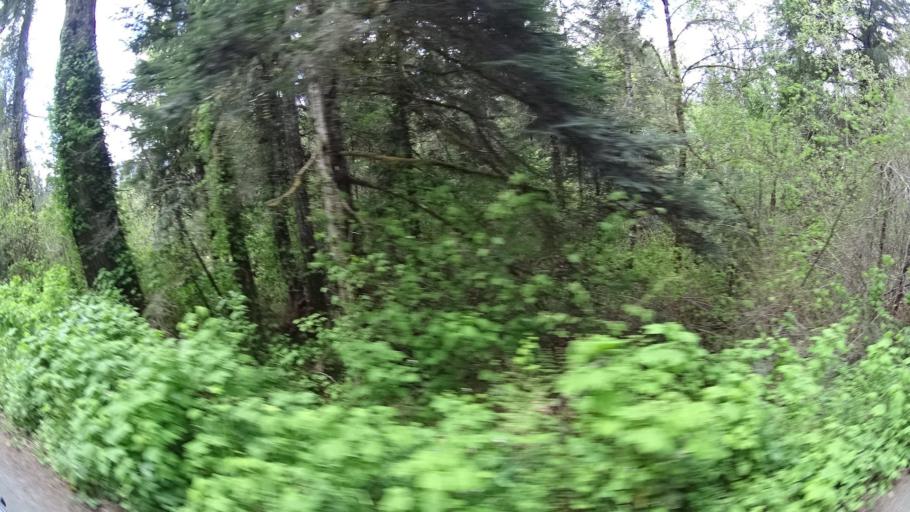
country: US
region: California
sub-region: Humboldt County
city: Blue Lake
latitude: 40.7686
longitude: -123.8755
